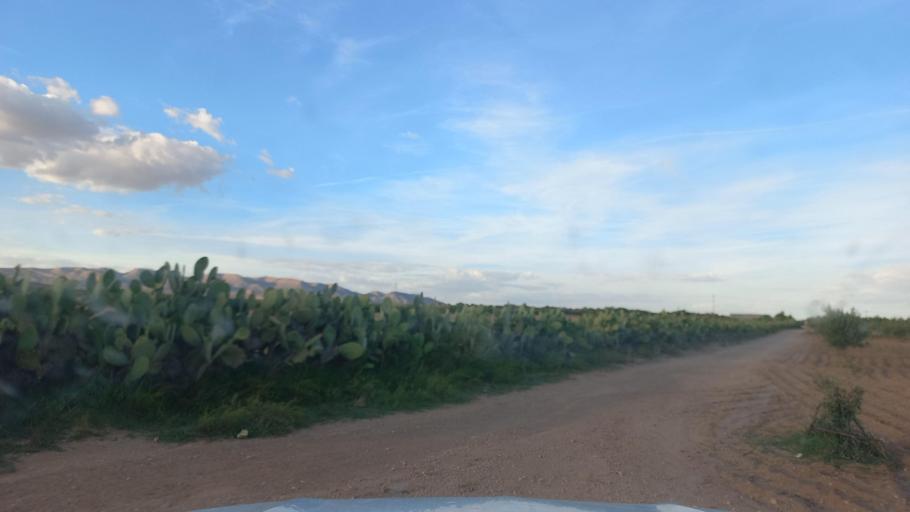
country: TN
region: Al Qasrayn
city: Sbiba
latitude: 35.3535
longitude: 9.0319
